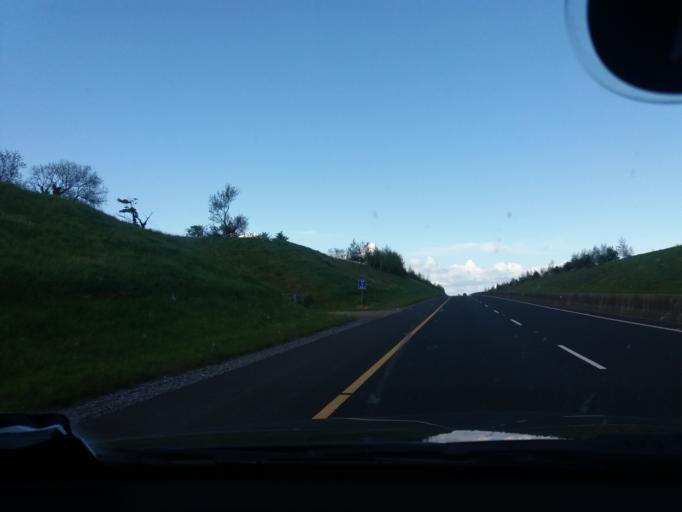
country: IE
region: Leinster
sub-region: County Carlow
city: Bagenalstown
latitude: 52.6552
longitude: -7.0904
